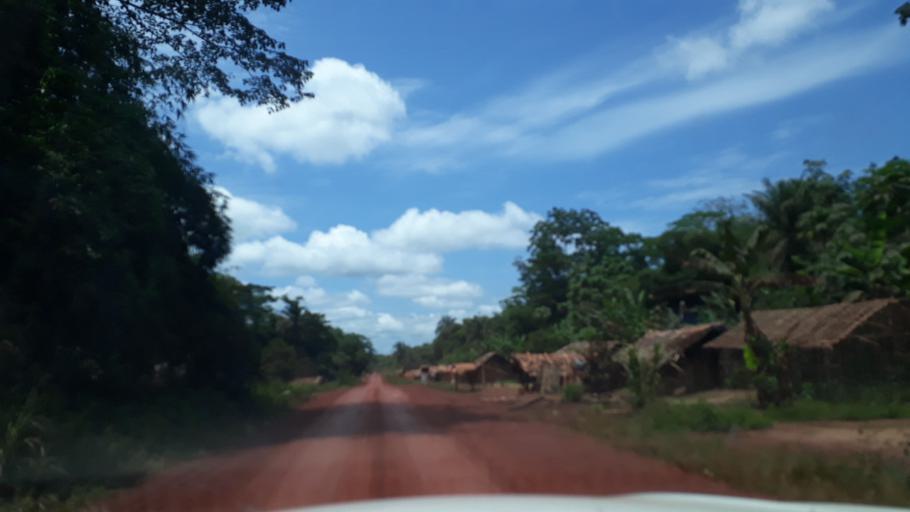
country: CD
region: Eastern Province
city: Kisangani
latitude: 0.5553
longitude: 25.8431
